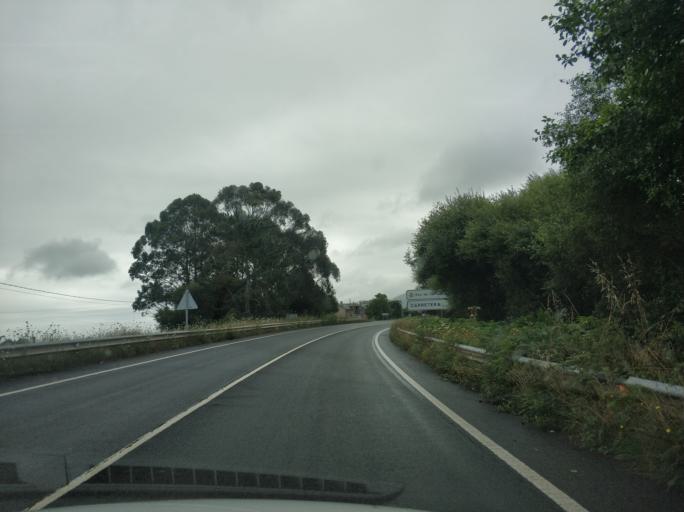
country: ES
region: Asturias
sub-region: Province of Asturias
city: Tineo
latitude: 43.5462
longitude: -6.4361
